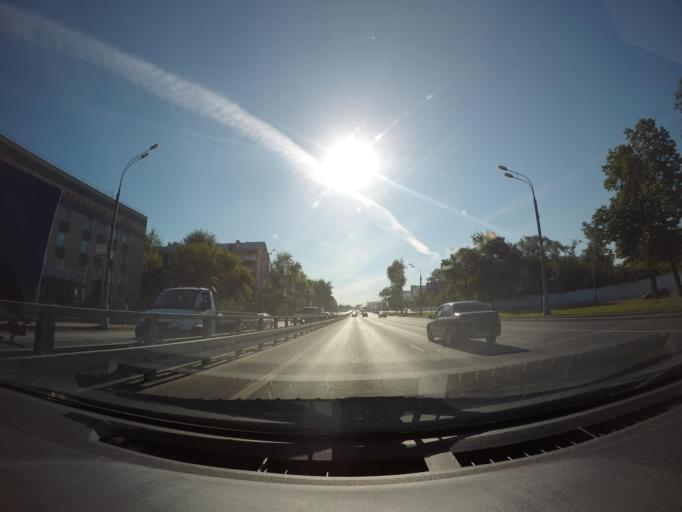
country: RU
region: Moscow
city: Ryazanskiy
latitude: 55.7307
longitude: 37.7411
